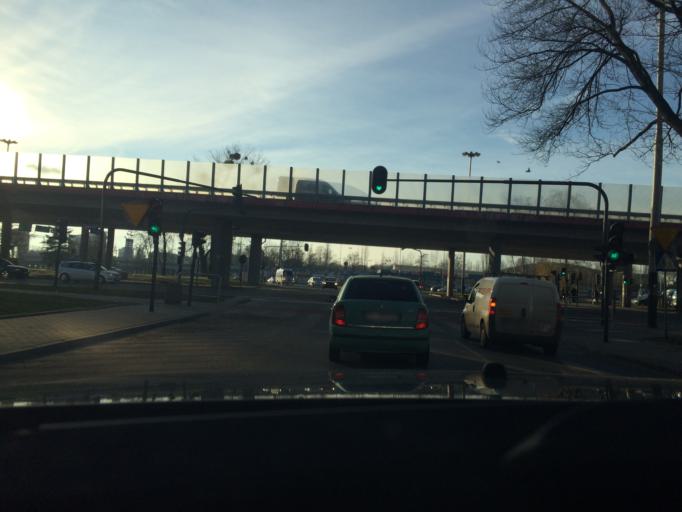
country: PL
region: Lodz Voivodeship
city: Lodz
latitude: 51.7582
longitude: 19.4345
